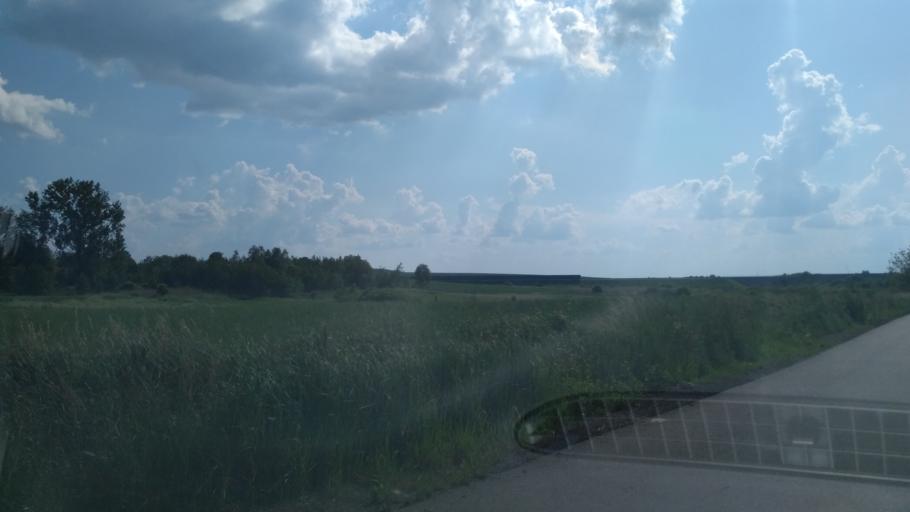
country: PL
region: Subcarpathian Voivodeship
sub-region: Powiat jaroslawski
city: Ostrow
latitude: 49.9272
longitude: 22.7385
